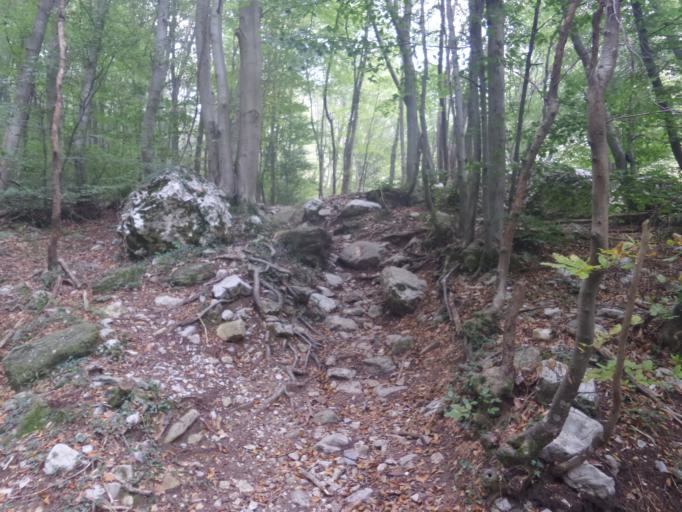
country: IT
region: Lombardy
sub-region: Provincia di Como
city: Osigo
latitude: 45.8479
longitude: 9.3031
